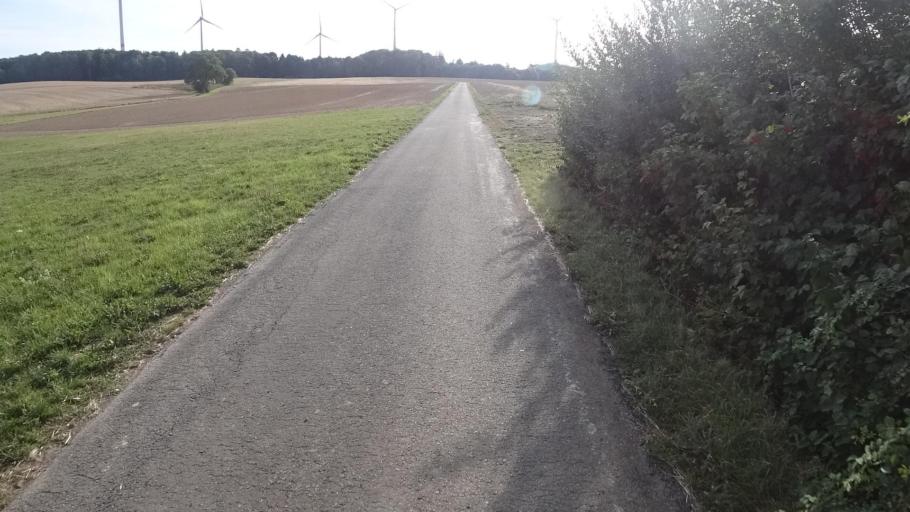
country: DE
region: Rheinland-Pfalz
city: Neuerkirch
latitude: 50.0154
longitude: 7.5019
